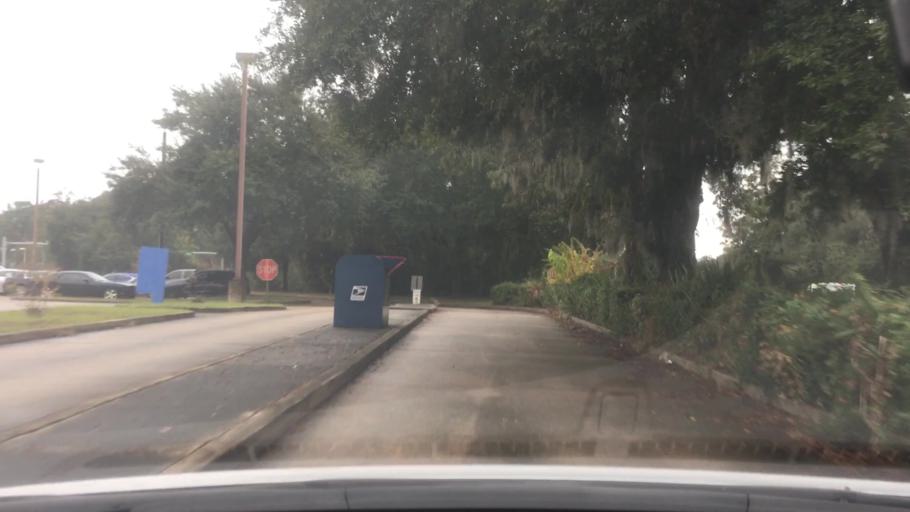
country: US
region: Florida
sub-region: Duval County
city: Atlantic Beach
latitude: 30.3585
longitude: -81.5169
